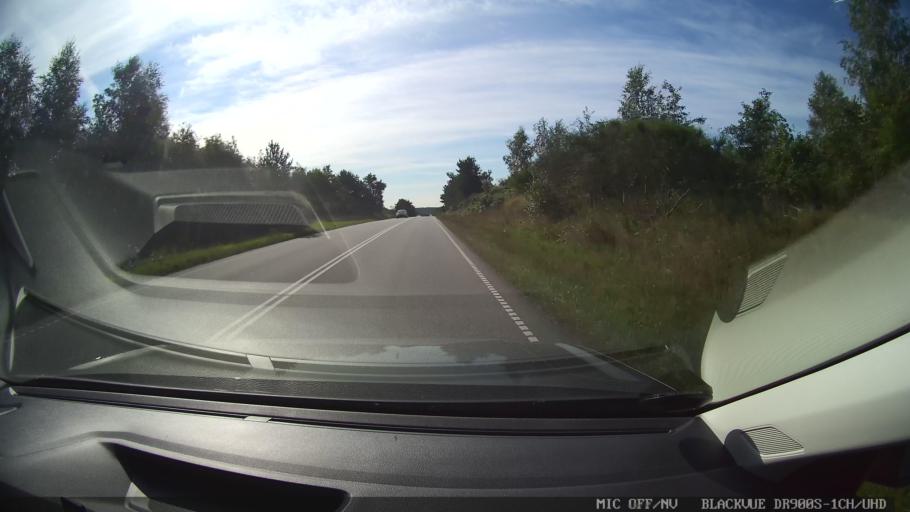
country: DK
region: North Denmark
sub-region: Mariagerfjord Kommune
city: Hadsund
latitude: 56.7530
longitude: 10.0720
